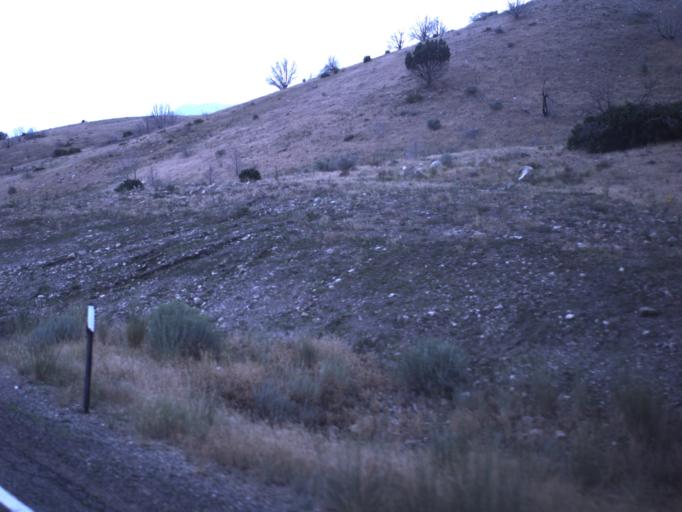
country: US
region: Utah
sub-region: Sanpete County
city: Fountain Green
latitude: 39.7026
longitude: -111.7026
